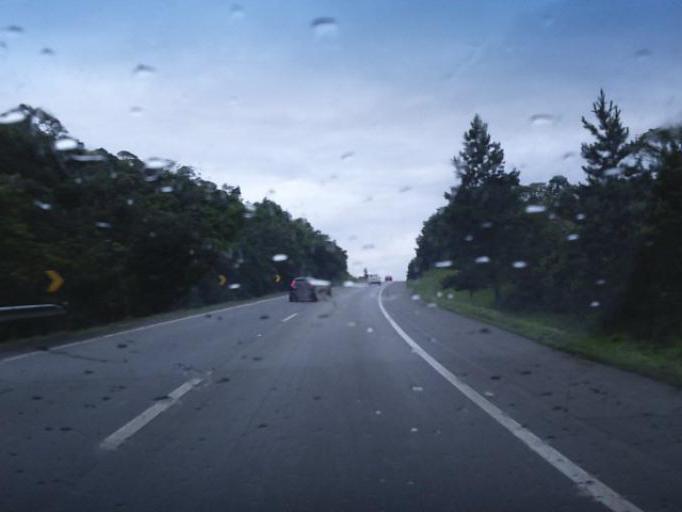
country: BR
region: Parana
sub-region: Sao Jose Dos Pinhais
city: Sao Jose dos Pinhais
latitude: -25.8497
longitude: -49.0130
